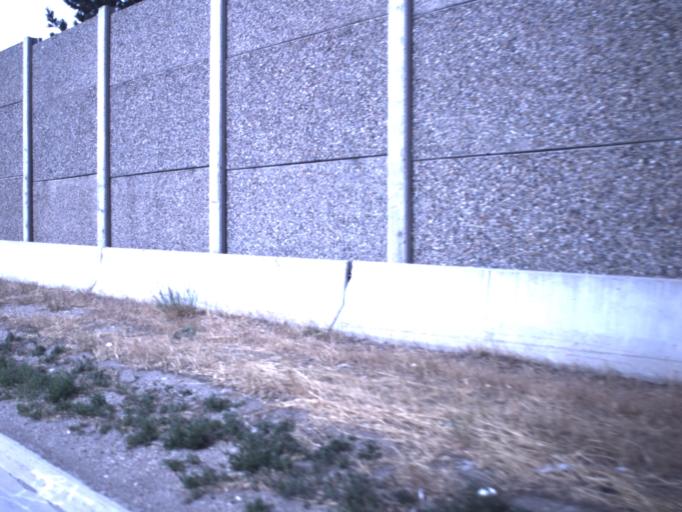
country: US
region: Utah
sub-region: Salt Lake County
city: South Jordan Heights
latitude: 40.5771
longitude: -111.9773
